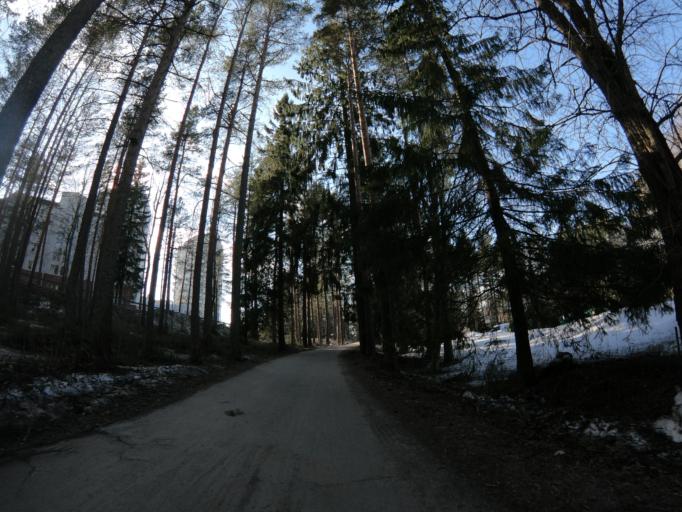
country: SE
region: Vaesterbotten
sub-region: Umea Kommun
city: Umea
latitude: 63.8462
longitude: 20.2974
